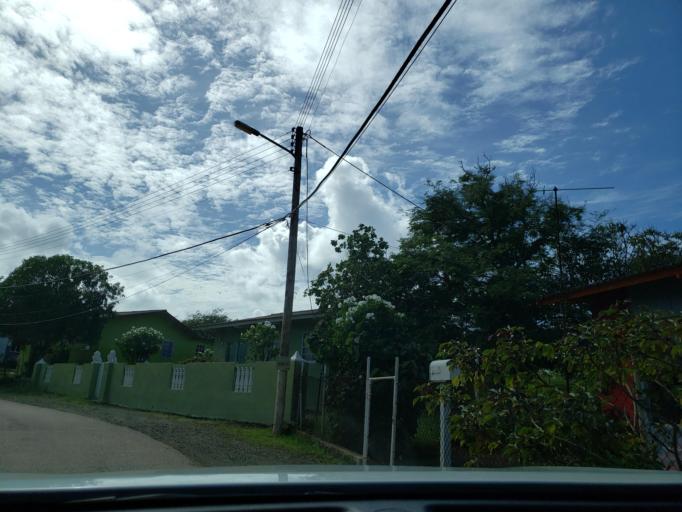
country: CW
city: Dorp Soto
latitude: 12.3714
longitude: -69.1526
